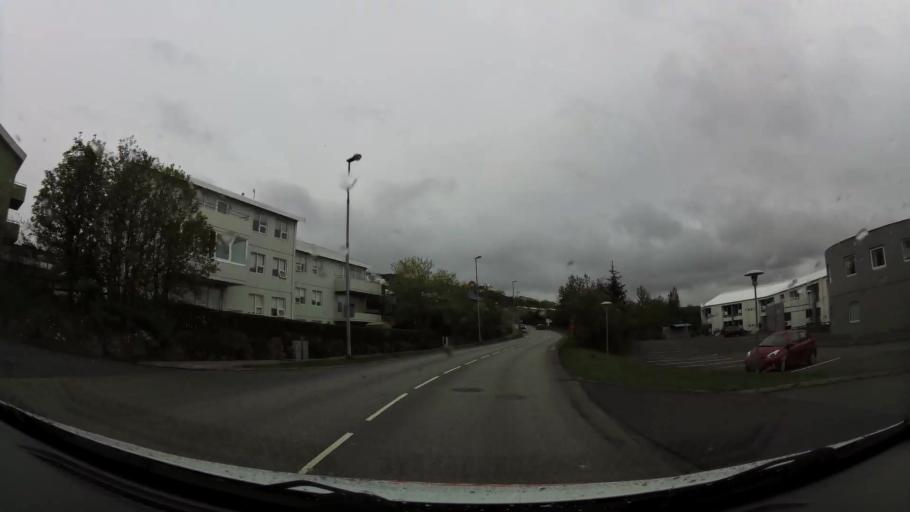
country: IS
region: Capital Region
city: Hafnarfjoerdur
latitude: 64.0657
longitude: -21.9310
